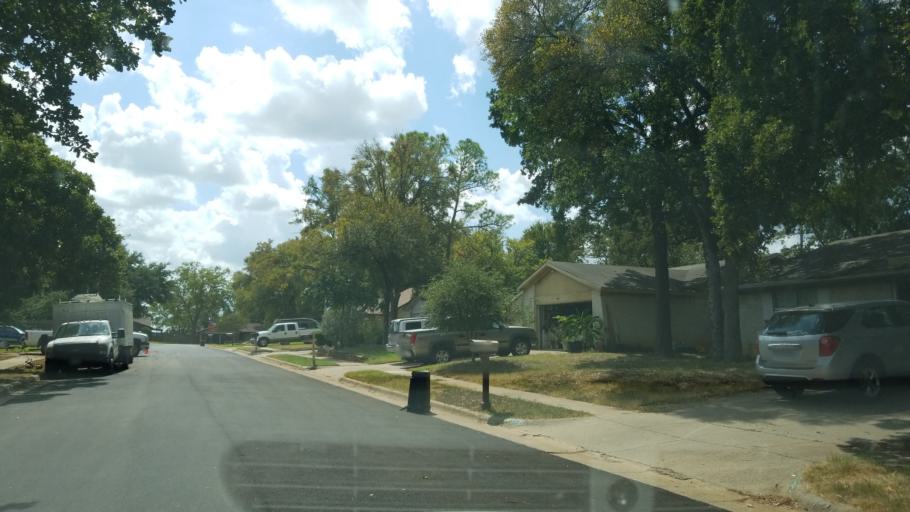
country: US
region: Texas
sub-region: Tarrant County
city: Euless
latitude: 32.8552
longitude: -97.0893
